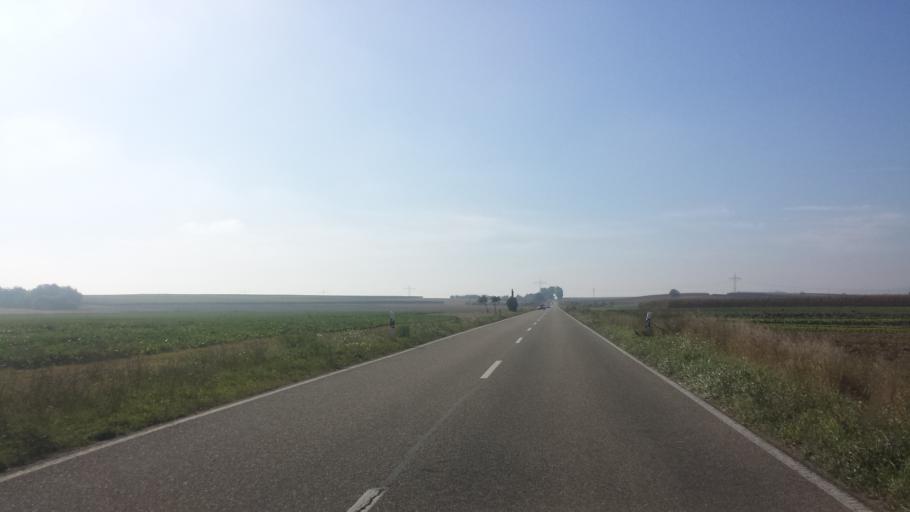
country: DE
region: Rheinland-Pfalz
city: Offenbach an der Queich
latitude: 49.1829
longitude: 8.1864
